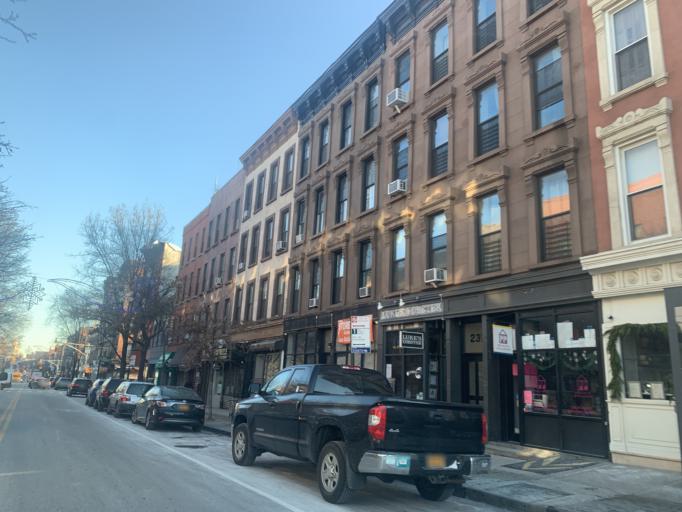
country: US
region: New York
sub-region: Kings County
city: Brooklyn
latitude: 40.6752
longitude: -73.9813
